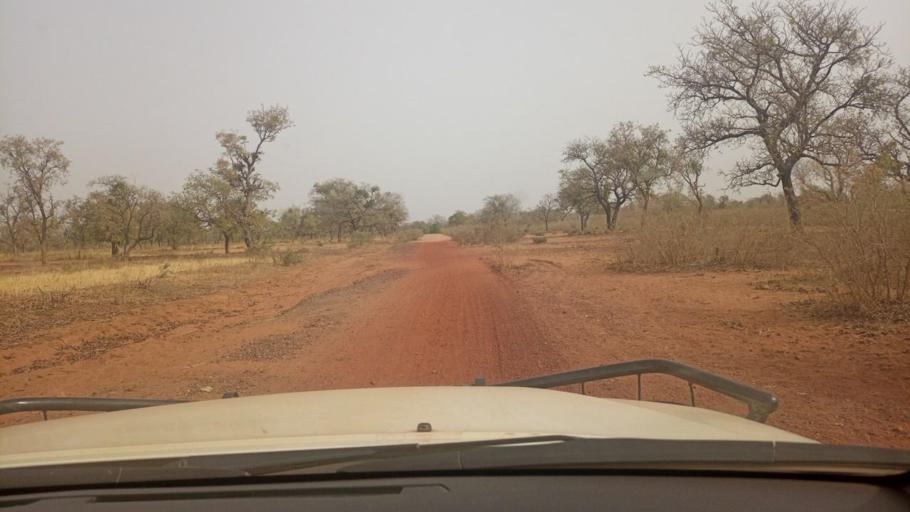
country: BF
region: Boucle du Mouhoun
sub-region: Province des Banwa
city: Salanso
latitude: 12.0979
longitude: -4.3326
